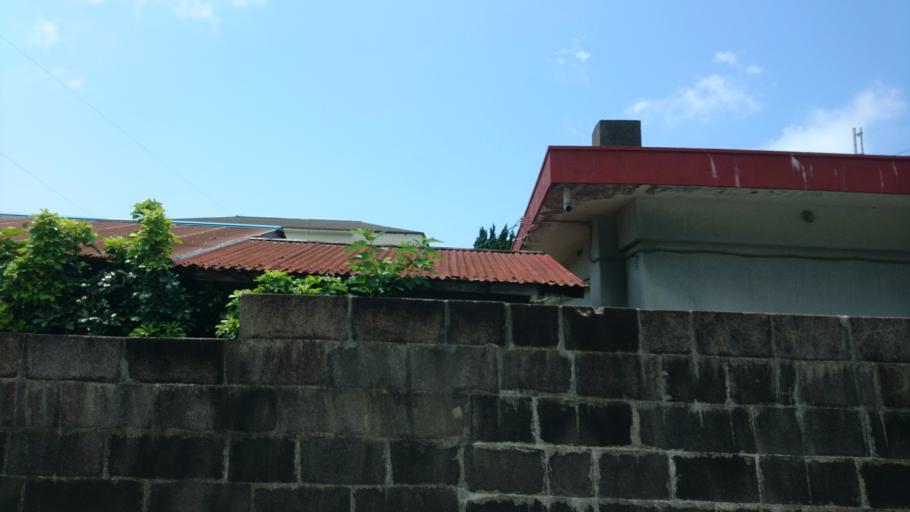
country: JP
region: Shizuoka
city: Shimoda
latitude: 34.4223
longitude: 139.2832
